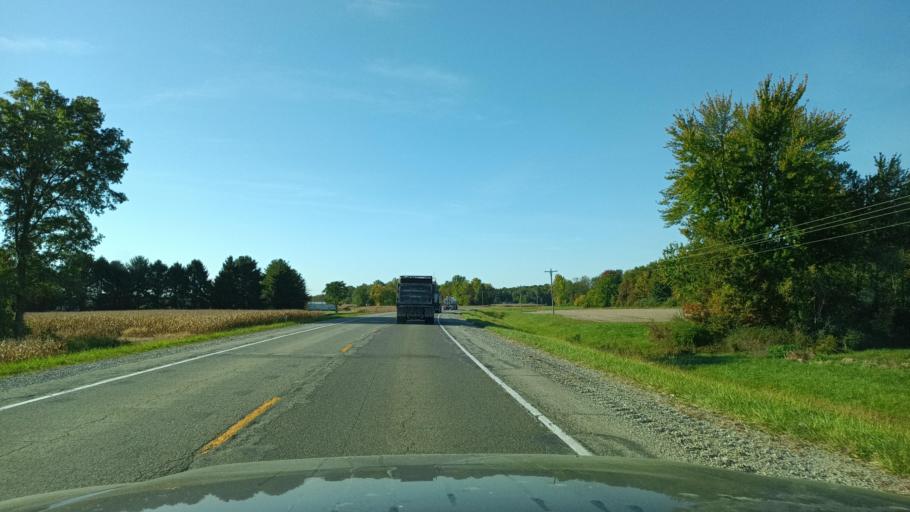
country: US
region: Illinois
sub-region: Clark County
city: Marshall
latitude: 39.4467
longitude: -87.6823
